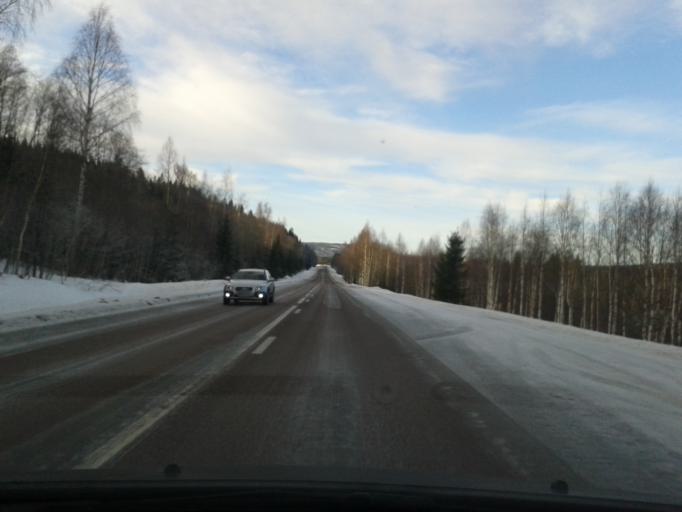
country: SE
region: Vaesternorrland
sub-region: OErnskoeldsviks Kommun
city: Bjasta
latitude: 63.3481
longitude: 18.4986
